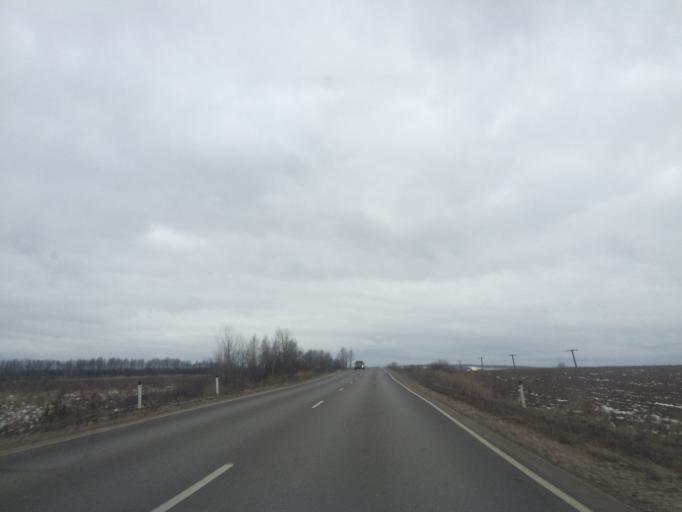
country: RU
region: Tula
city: Krapivna
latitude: 54.1145
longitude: 37.1849
